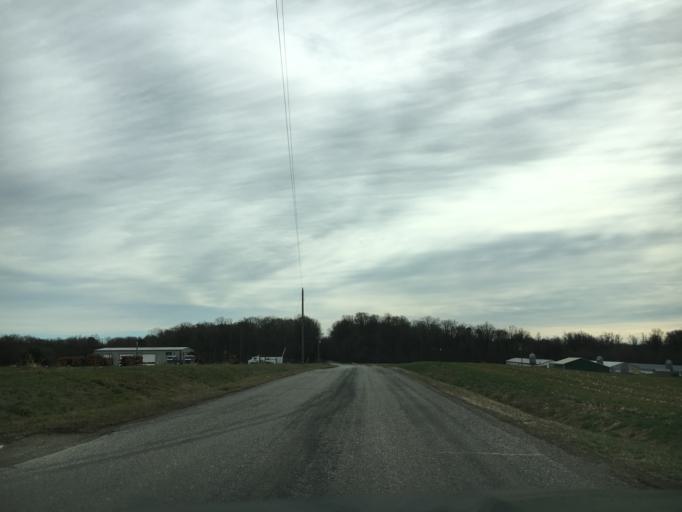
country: US
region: Virginia
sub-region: Amelia County
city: Amelia Court House
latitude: 37.4373
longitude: -78.0205
